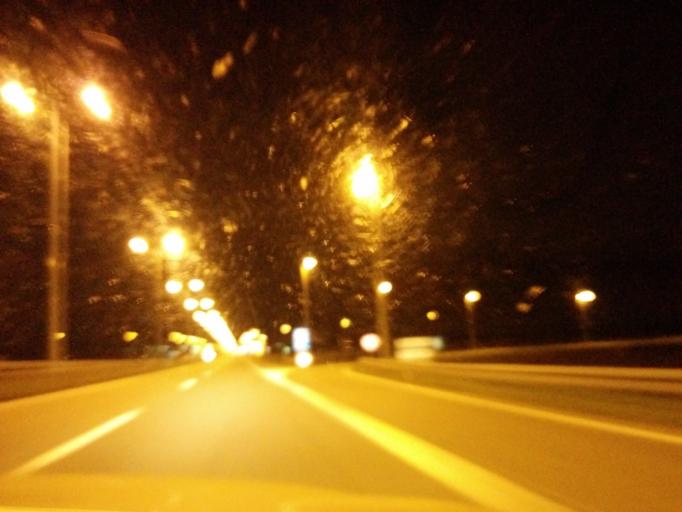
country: RS
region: Autonomna Pokrajina Vojvodina
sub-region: Sremski Okrug
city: Sid
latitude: 45.0482
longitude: 19.2078
